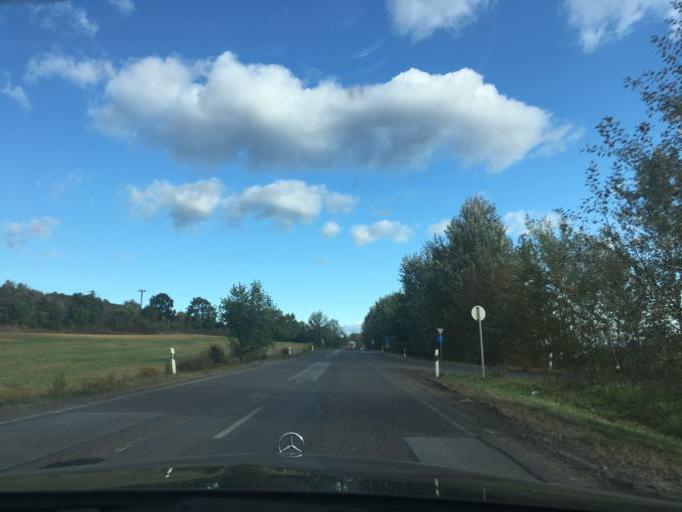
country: HU
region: Borsod-Abauj-Zemplen
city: Encs
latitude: 48.4227
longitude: 21.1799
